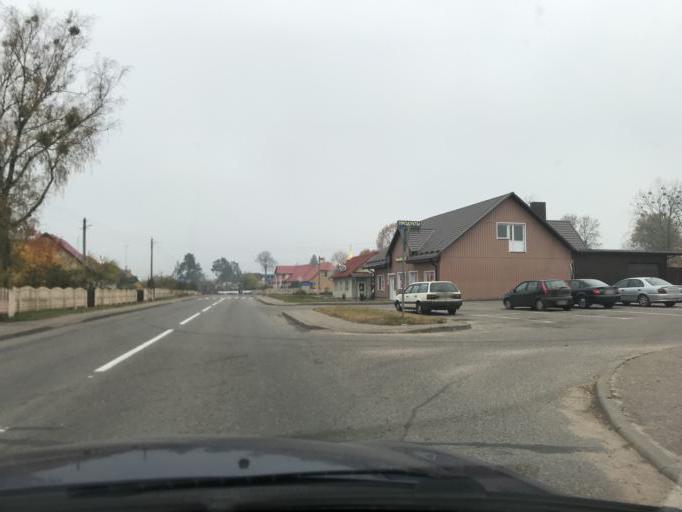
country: BY
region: Grodnenskaya
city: Hrodna
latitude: 53.8164
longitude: 23.8630
